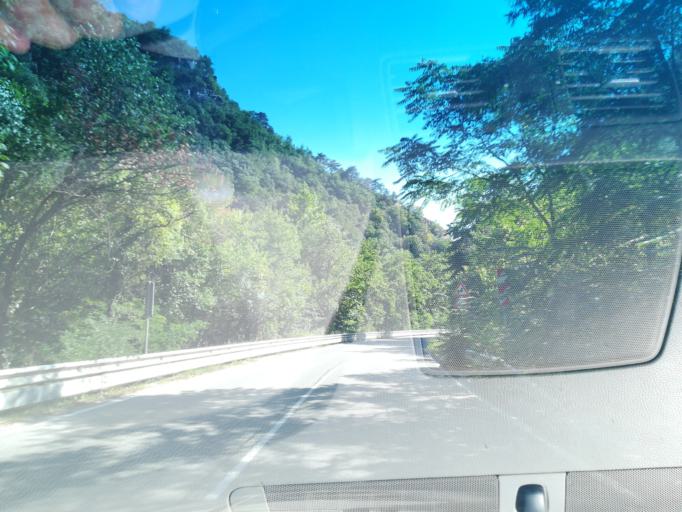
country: BG
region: Plovdiv
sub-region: Obshtina Asenovgrad
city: Asenovgrad
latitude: 41.9741
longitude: 24.8667
